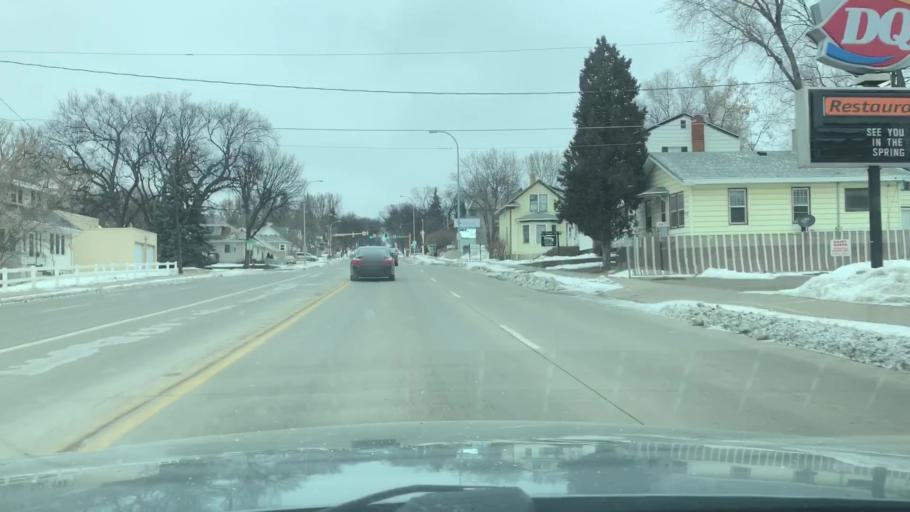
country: US
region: North Dakota
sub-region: Burleigh County
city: Bismarck
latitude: 46.8069
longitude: -100.7943
